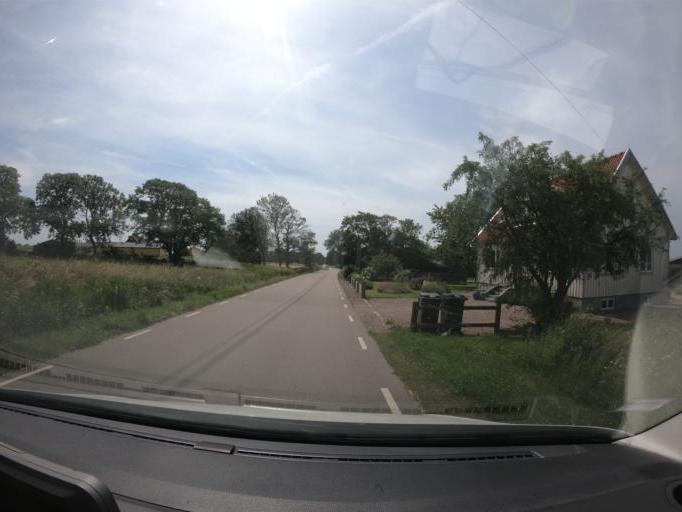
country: SE
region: Skane
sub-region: Angelholms Kommun
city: Vejbystrand
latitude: 56.4021
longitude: 12.7220
